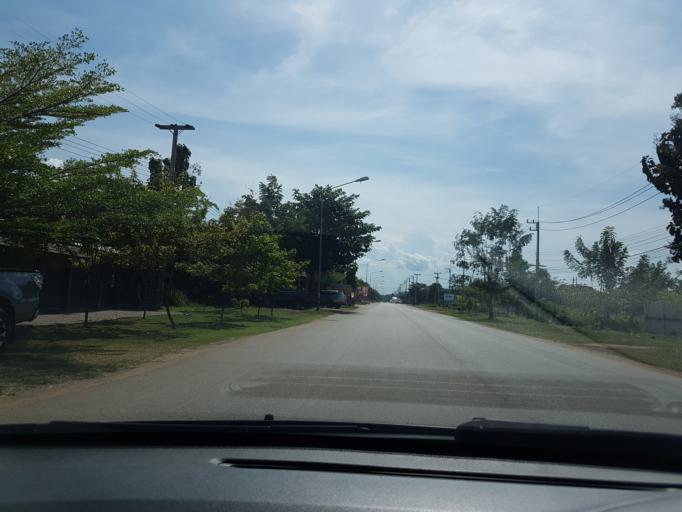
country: TH
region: Lampang
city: Ko Kha
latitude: 18.2145
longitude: 99.3898
